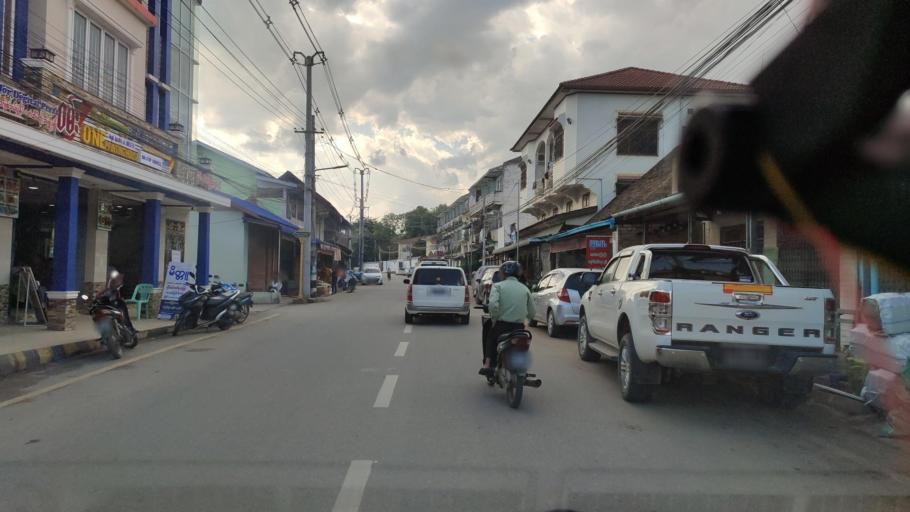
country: TH
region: Chiang Rai
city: Mae Sai
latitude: 21.2903
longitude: 99.6096
